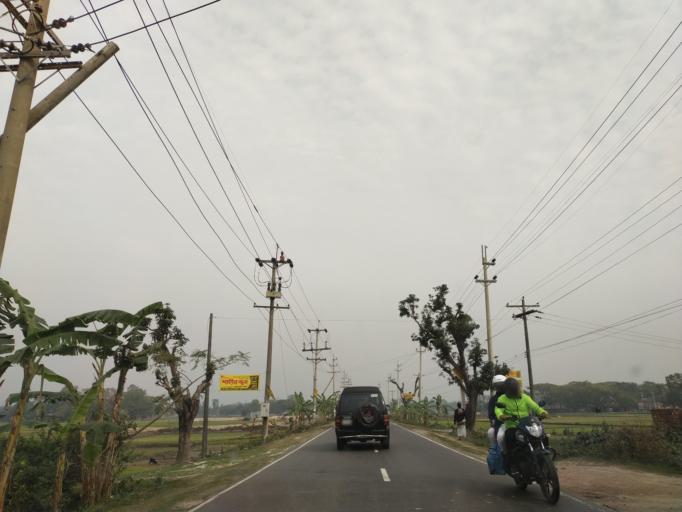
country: BD
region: Dhaka
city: Narsingdi
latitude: 23.9885
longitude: 90.7357
